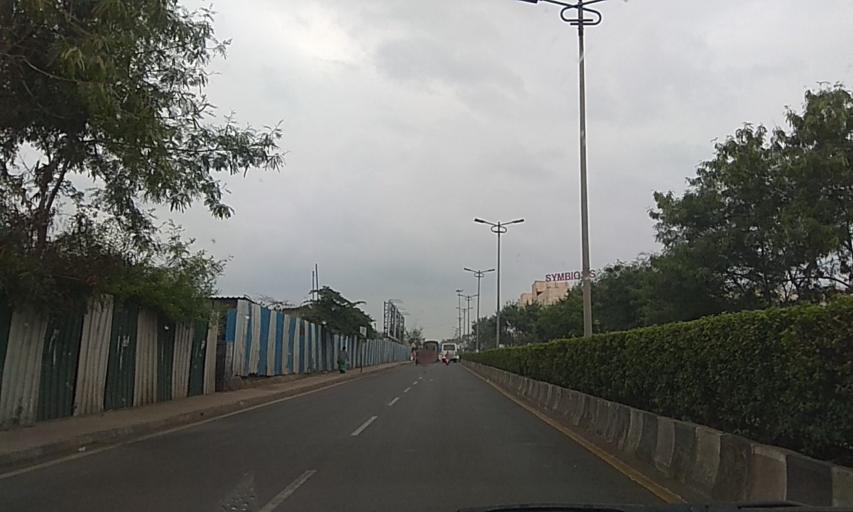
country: IN
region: Maharashtra
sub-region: Pune Division
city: Lohogaon
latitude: 18.5741
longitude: 73.9075
